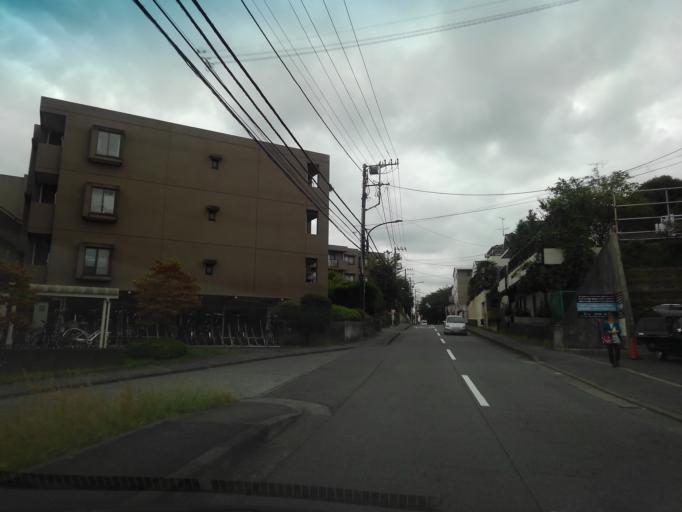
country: JP
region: Tokyo
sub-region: Machida-shi
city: Machida
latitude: 35.5775
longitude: 139.3988
